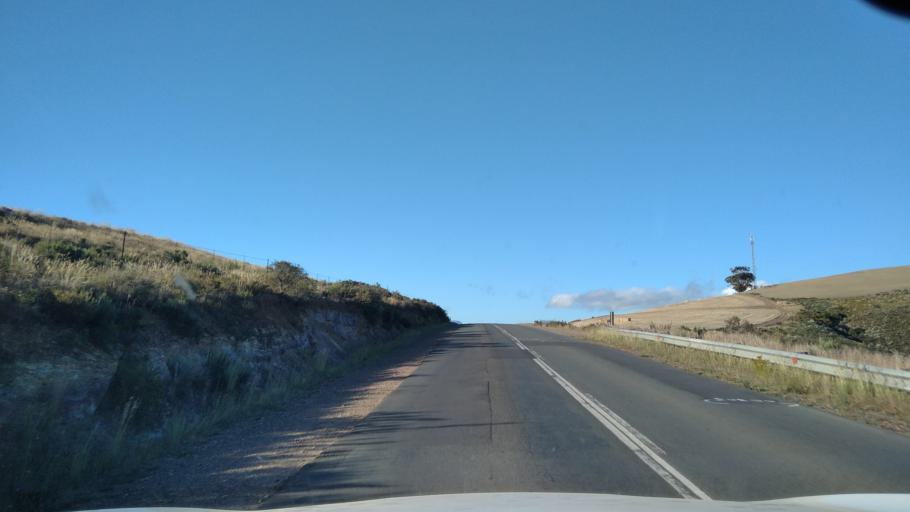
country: ZA
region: Western Cape
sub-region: Overberg District Municipality
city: Caledon
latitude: -34.1511
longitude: 19.2995
